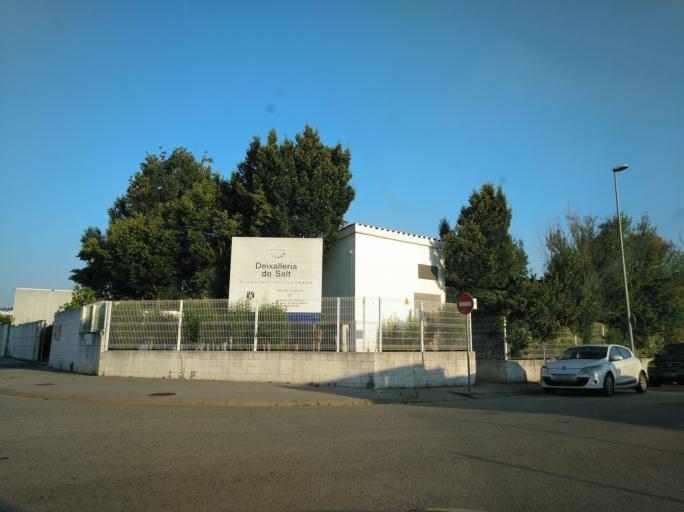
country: ES
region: Catalonia
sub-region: Provincia de Girona
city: Vilablareix
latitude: 41.9684
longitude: 2.7751
